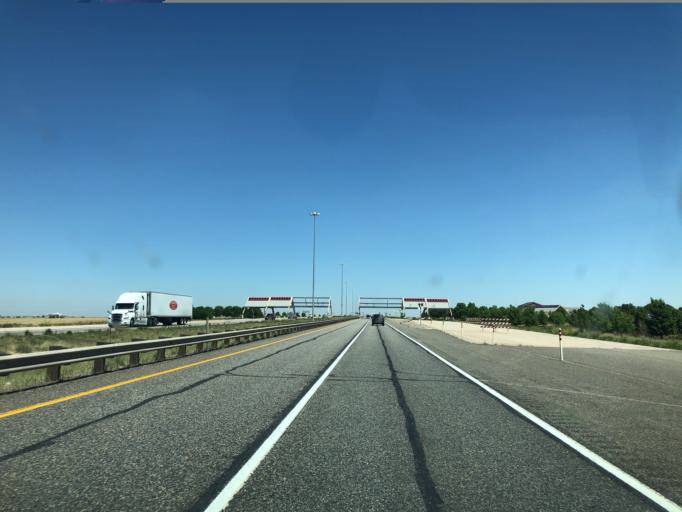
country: US
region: Colorado
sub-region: Adams County
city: Aurora
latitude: 39.7678
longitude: -104.7164
